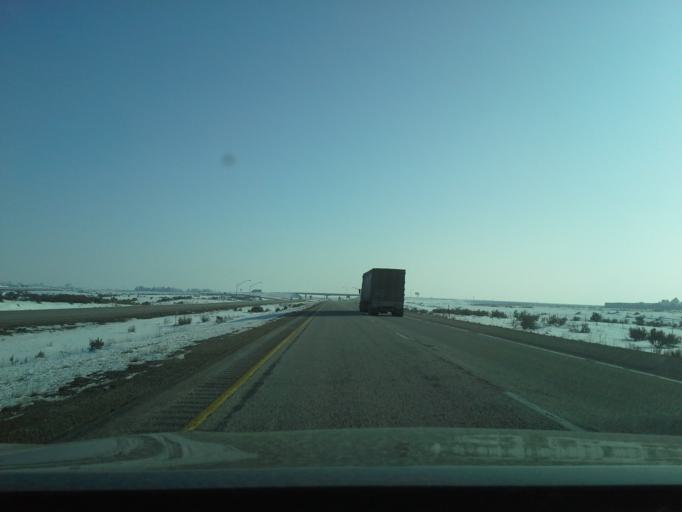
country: US
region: Idaho
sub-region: Oneida County
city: Malad City
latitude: 42.5096
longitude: -112.1700
